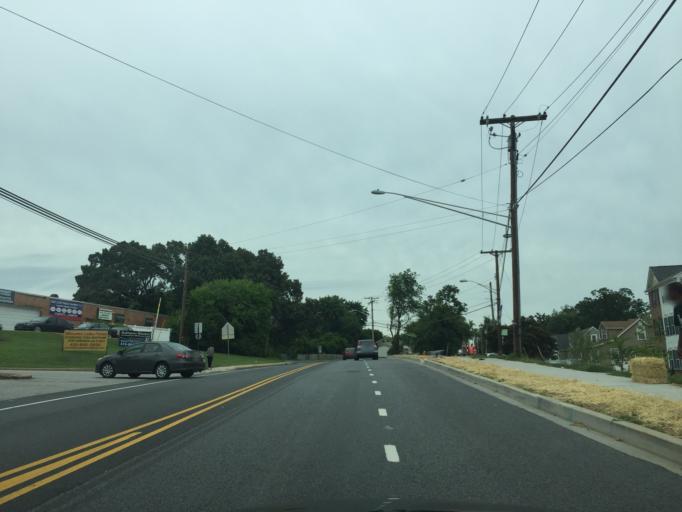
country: US
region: Maryland
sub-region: Baltimore County
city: Rosedale
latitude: 39.3414
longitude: -76.5050
